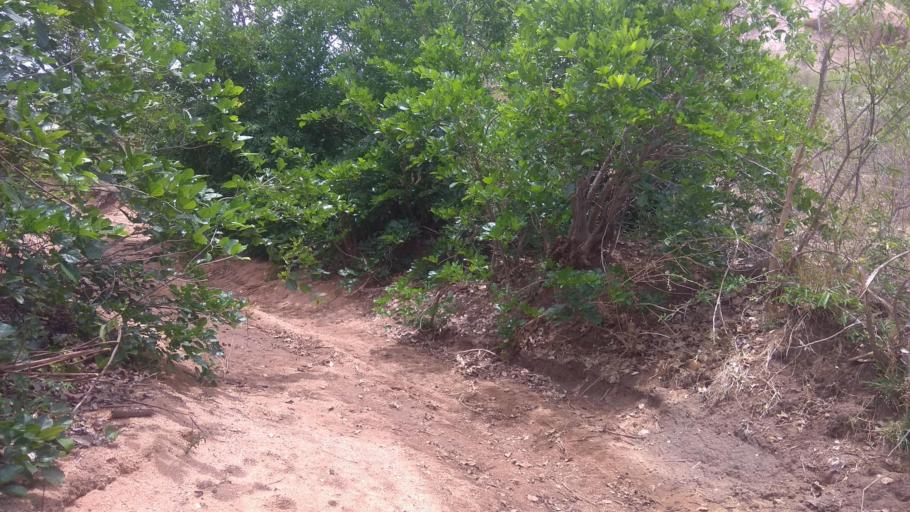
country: IN
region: Telangana
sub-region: Mahbubnagar
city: Farrukhnagar
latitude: 16.8876
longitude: 78.5033
